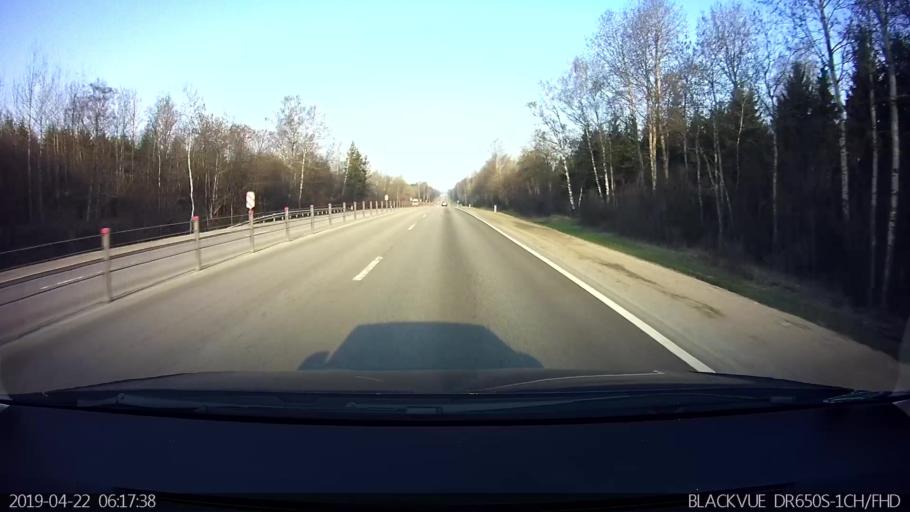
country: RU
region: Moskovskaya
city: Mozhaysk
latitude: 55.4620
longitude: 35.9848
